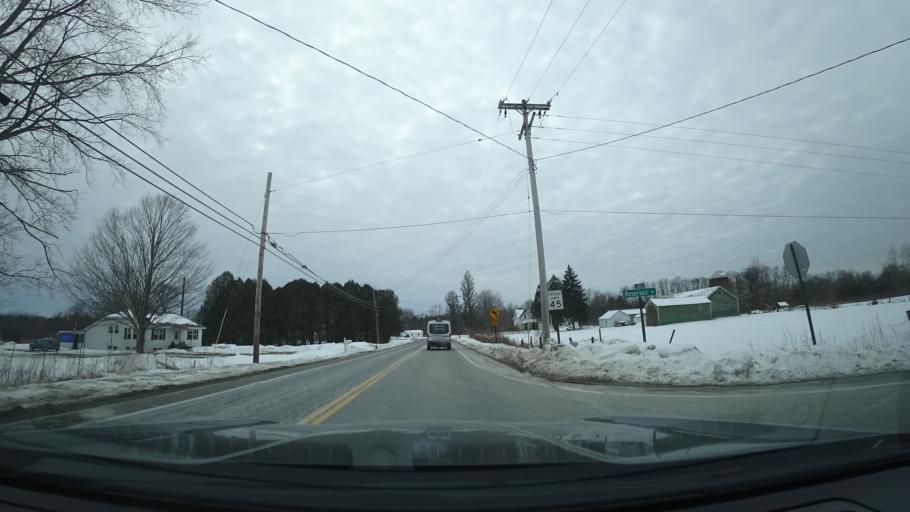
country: US
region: New York
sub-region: Washington County
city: Fort Edward
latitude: 43.2662
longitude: -73.6088
